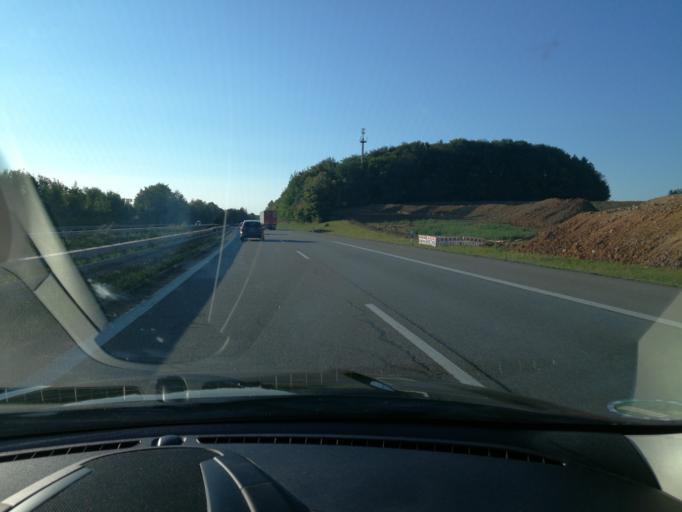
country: DE
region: Bavaria
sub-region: Upper Palatinate
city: Brunn
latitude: 49.0852
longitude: 11.8975
